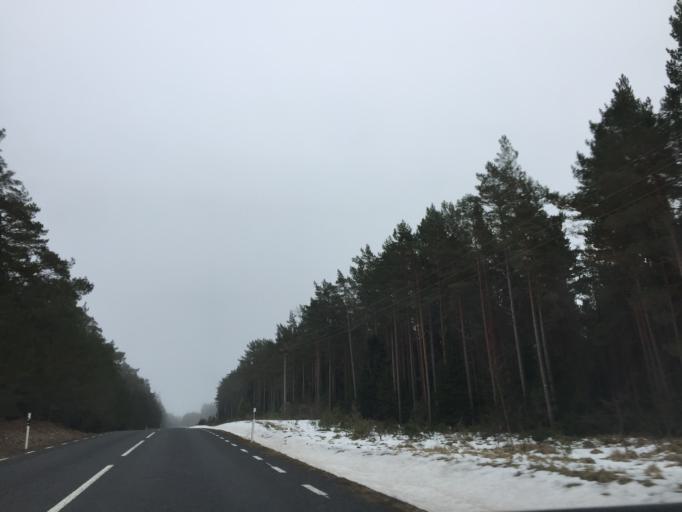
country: EE
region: Saare
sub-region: Kuressaare linn
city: Kuressaare
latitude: 58.4683
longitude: 22.0364
